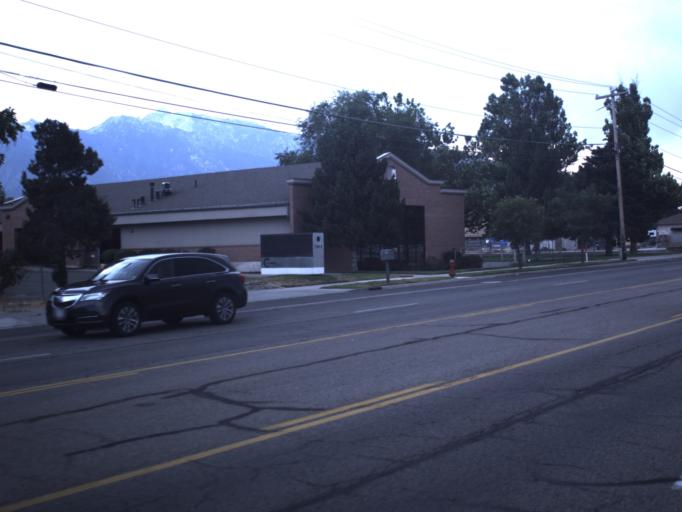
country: US
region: Utah
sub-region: Salt Lake County
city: Sandy City
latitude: 40.6069
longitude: -111.8723
